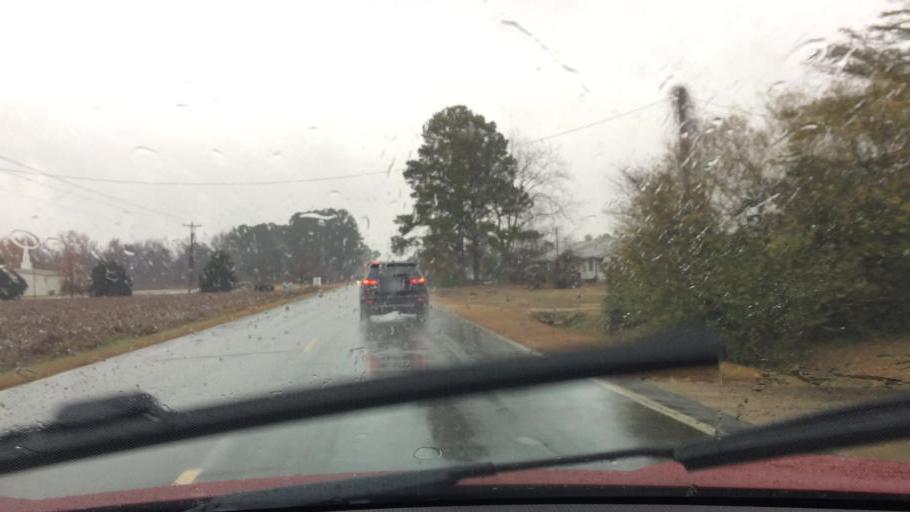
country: US
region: North Carolina
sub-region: Wayne County
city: Elroy
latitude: 35.4093
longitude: -77.9269
